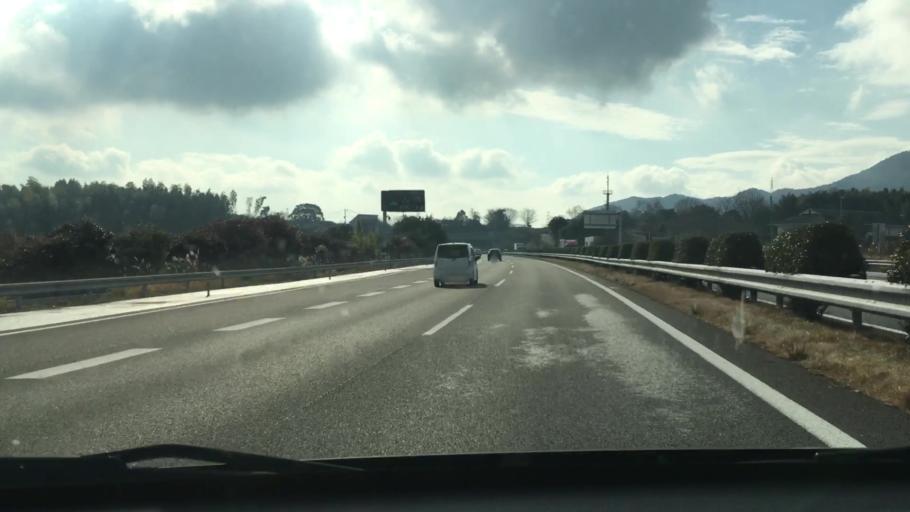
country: JP
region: Kumamoto
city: Uto
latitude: 32.6934
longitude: 130.7407
